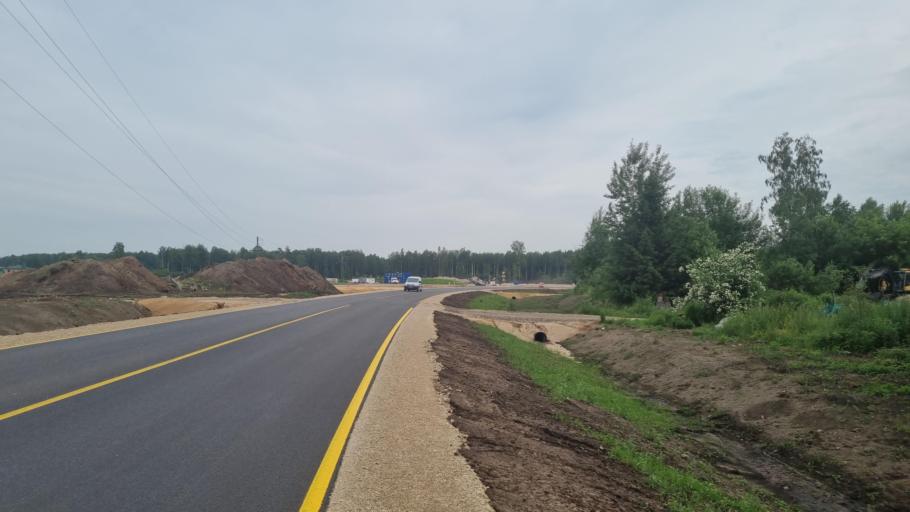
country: LV
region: Kekava
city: Balozi
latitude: 56.8737
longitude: 24.1663
